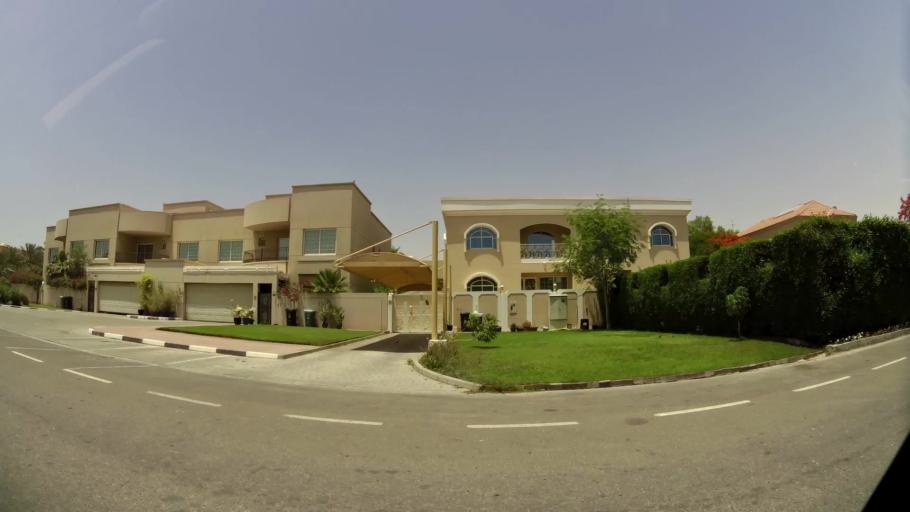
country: AE
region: Dubai
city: Dubai
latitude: 25.1662
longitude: 55.2217
